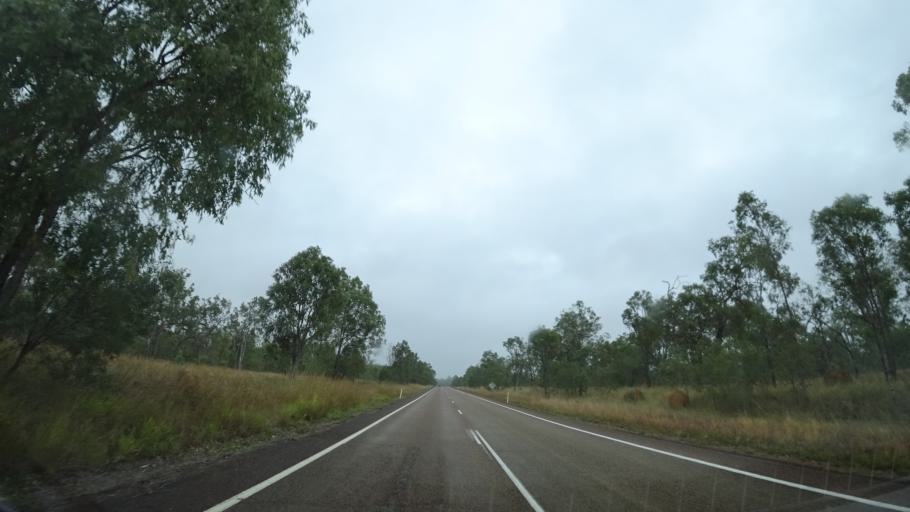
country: AU
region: Queensland
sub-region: Tablelands
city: Ravenshoe
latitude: -17.6953
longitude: 145.2166
